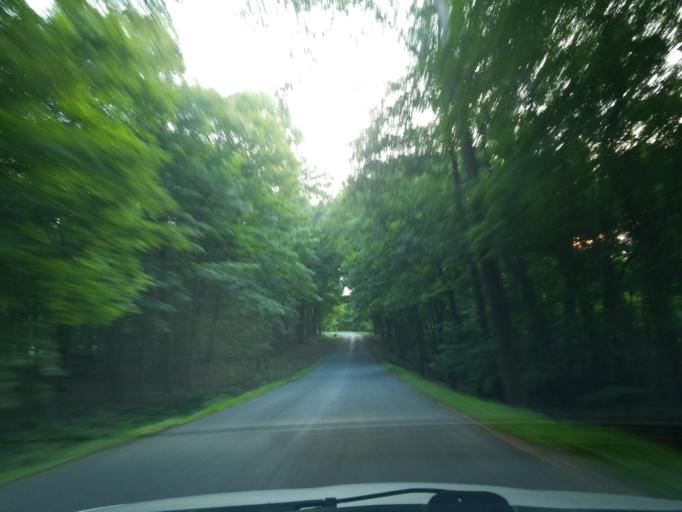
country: US
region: Minnesota
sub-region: Washington County
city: Stillwater
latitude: 45.0897
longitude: -92.7643
